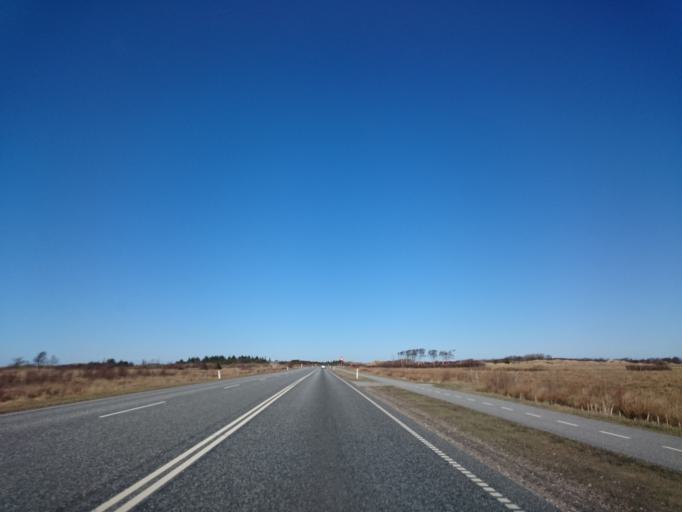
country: DK
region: North Denmark
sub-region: Frederikshavn Kommune
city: Skagen
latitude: 57.6679
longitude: 10.4544
